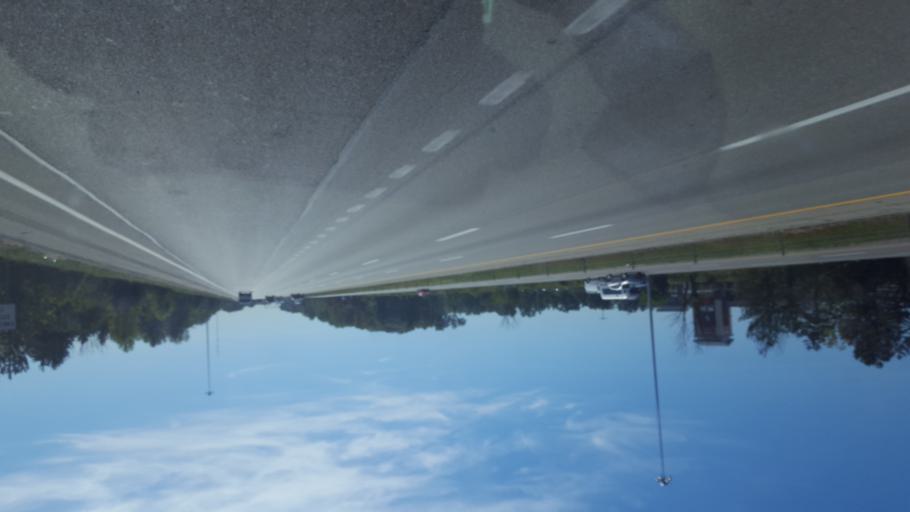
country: US
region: Ohio
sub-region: Delaware County
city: Sunbury
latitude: 40.2623
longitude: -82.9280
